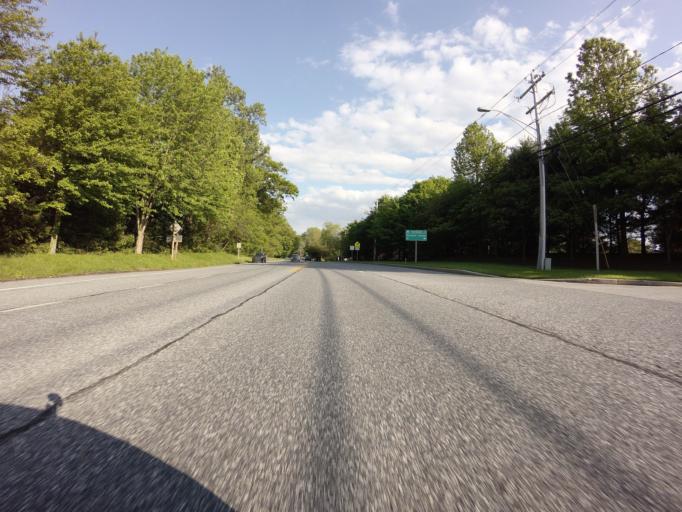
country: US
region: Maryland
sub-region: Baltimore County
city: Mays Chapel
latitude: 39.4368
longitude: -76.6825
